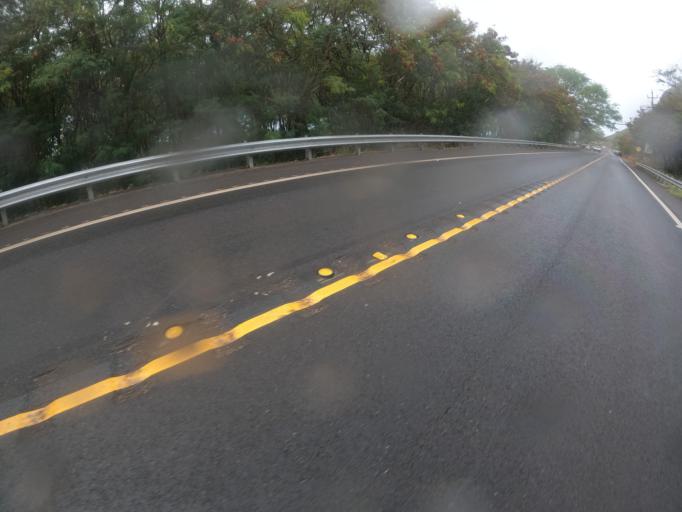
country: US
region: Hawaii
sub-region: Honolulu County
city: Makaha Valley
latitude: 21.5367
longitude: -158.2302
